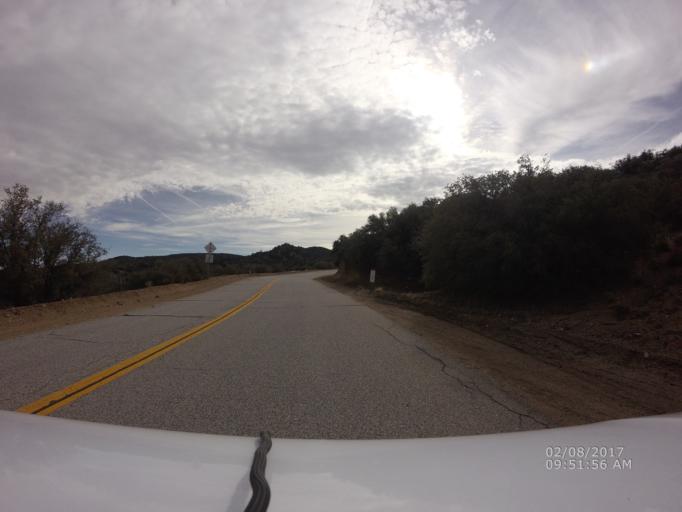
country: US
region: California
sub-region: San Bernardino County
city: Pinon Hills
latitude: 34.4285
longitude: -117.8092
